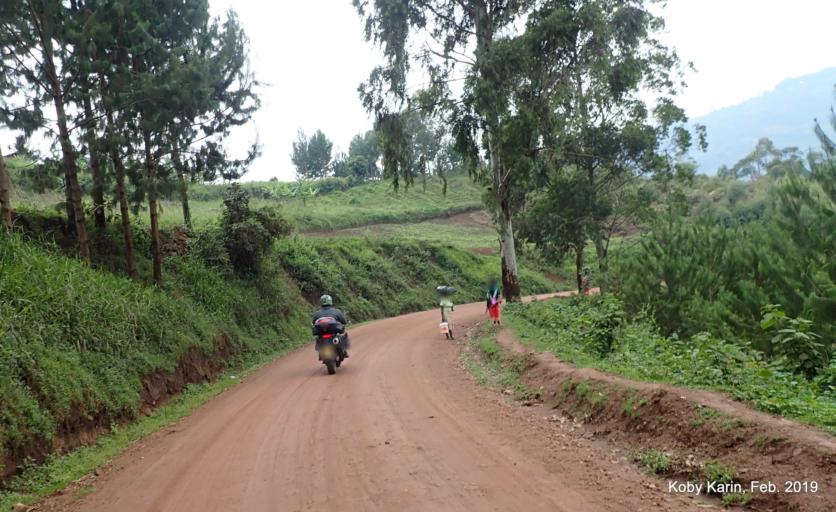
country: UG
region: Western Region
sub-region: Kabale District
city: Kabale
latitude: -1.2612
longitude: 29.9440
